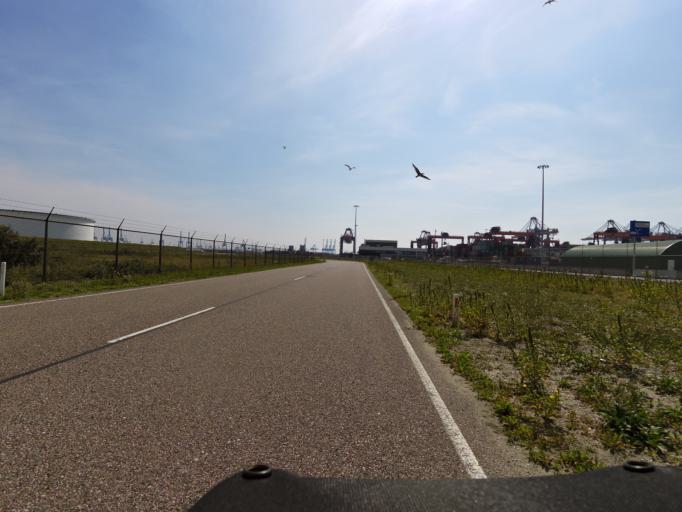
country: NL
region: South Holland
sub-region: Gemeente Rotterdam
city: Hoek van Holland
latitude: 51.9776
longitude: 4.0466
